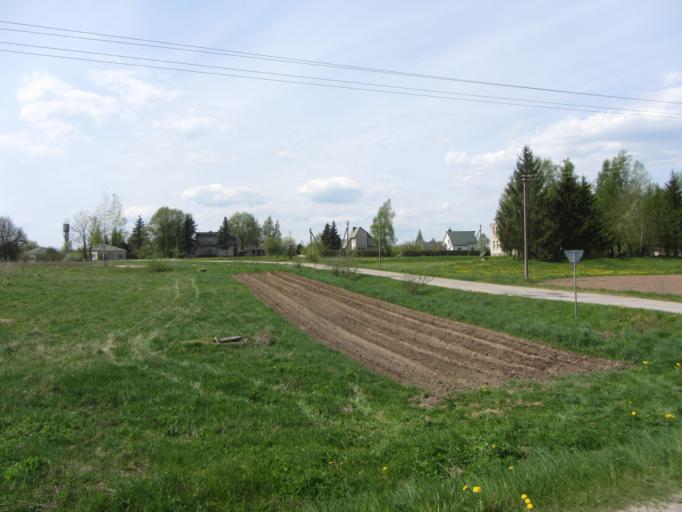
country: LT
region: Utenos apskritis
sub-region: Anyksciai
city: Anyksciai
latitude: 55.4906
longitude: 25.0974
